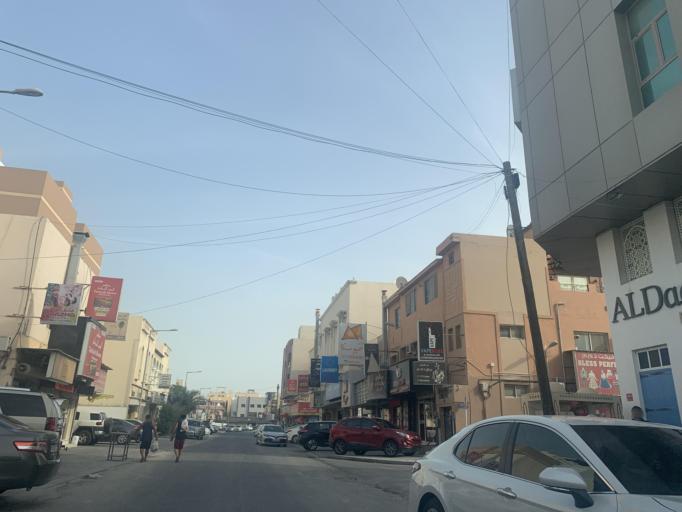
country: BH
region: Northern
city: Ar Rifa'
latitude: 26.1332
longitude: 50.5586
